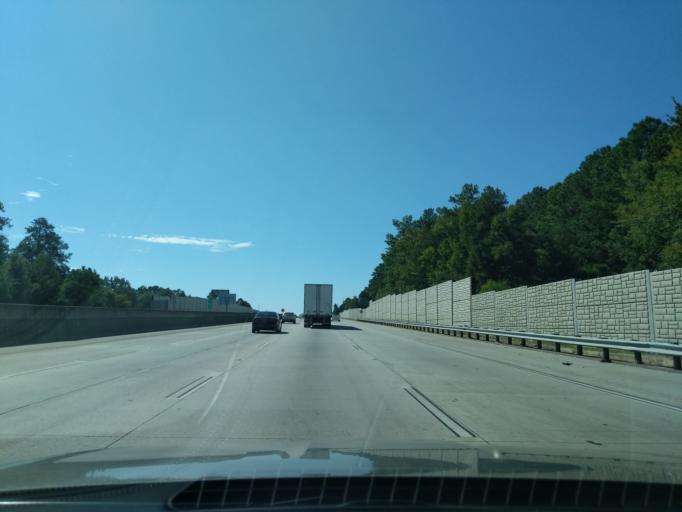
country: US
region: Georgia
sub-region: Columbia County
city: Martinez
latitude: 33.5071
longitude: -82.0504
